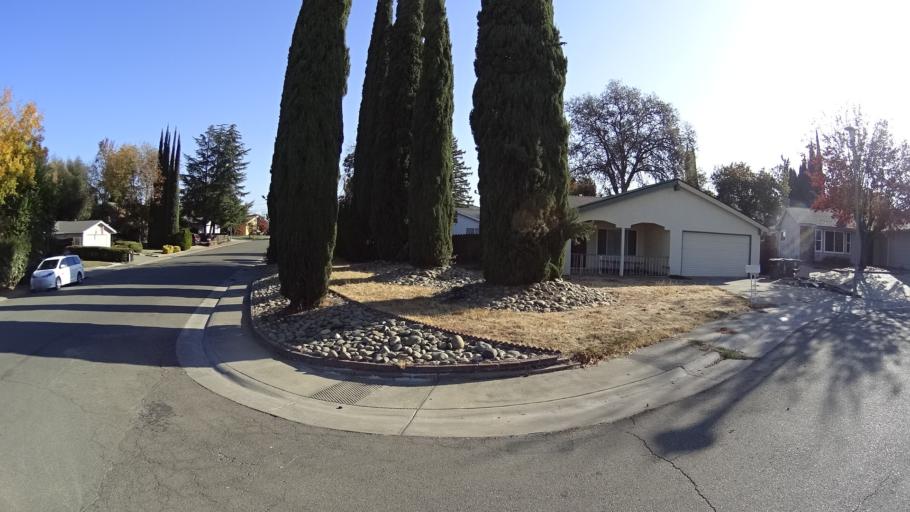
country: US
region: California
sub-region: Sacramento County
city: Citrus Heights
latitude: 38.6951
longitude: -121.2733
